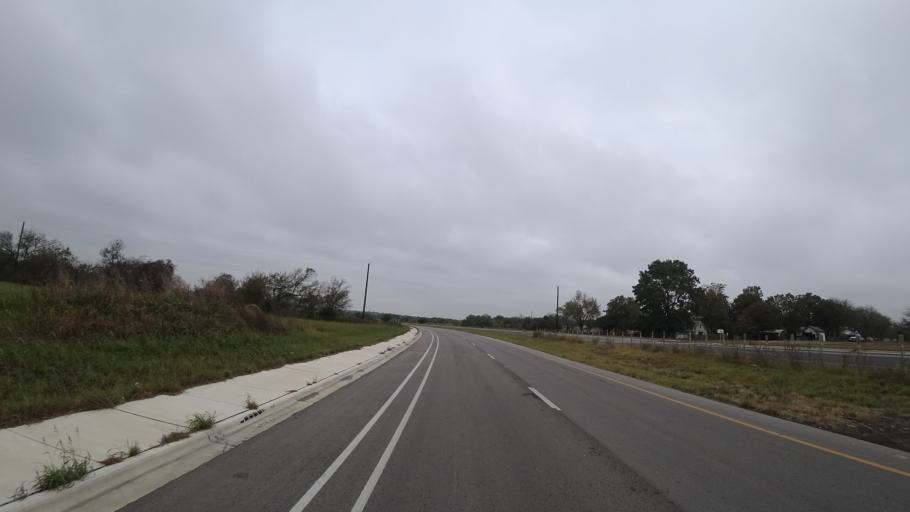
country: US
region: Texas
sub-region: Travis County
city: Pflugerville
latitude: 30.4180
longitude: -97.6134
